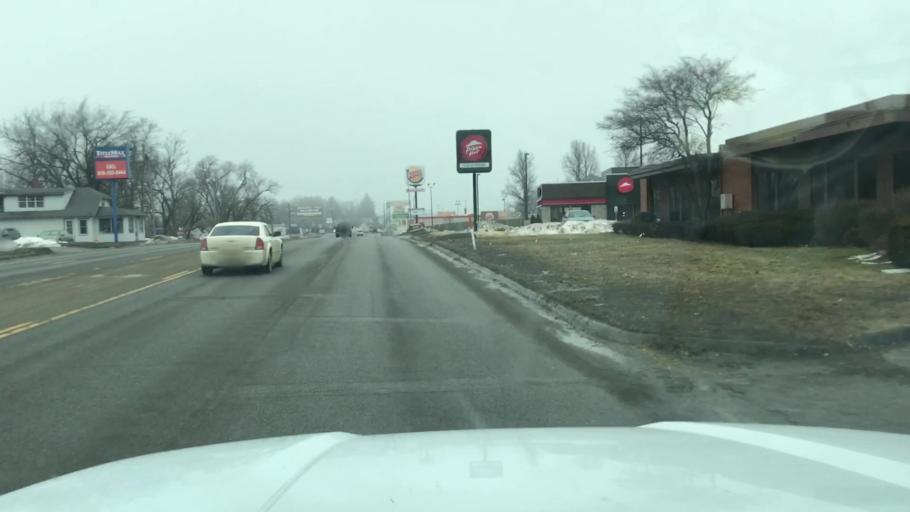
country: US
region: Missouri
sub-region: Buchanan County
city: Saint Joseph
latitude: 39.7512
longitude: -94.8030
